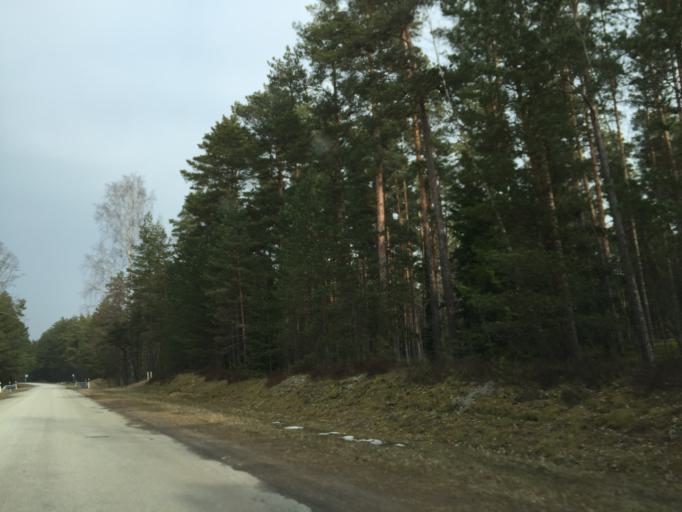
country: LV
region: Salacgrivas
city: Ainazi
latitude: 57.9655
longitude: 24.4071
